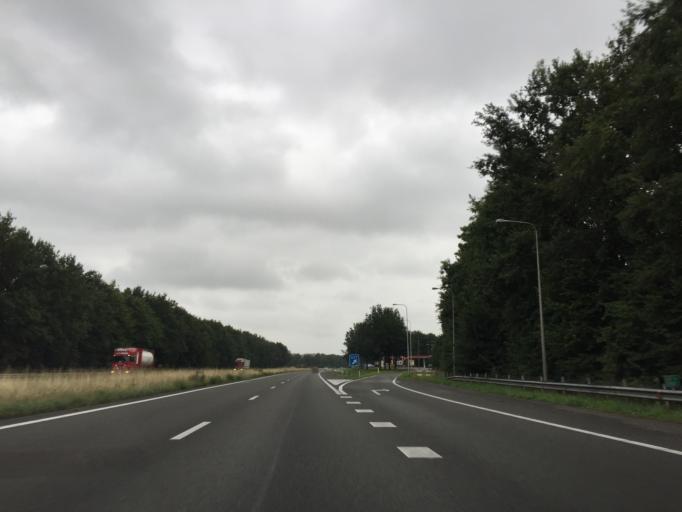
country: NL
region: Limburg
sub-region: Eijsden-Margraten
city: Eijsden
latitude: 50.7885
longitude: 5.7278
